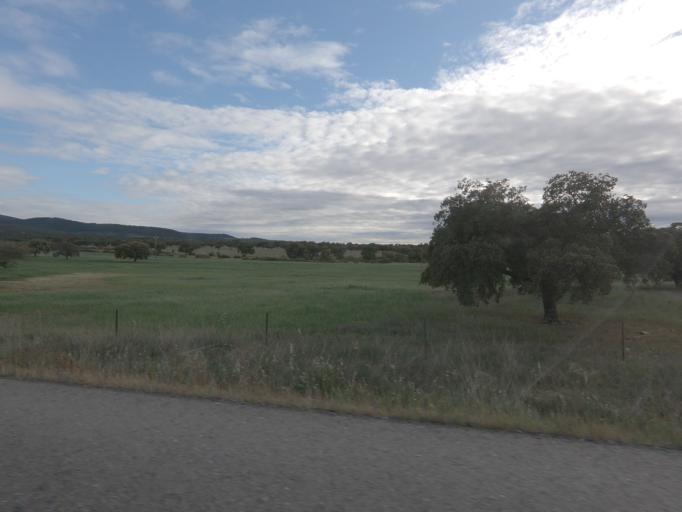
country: ES
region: Extremadura
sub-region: Provincia de Caceres
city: Pedroso de Acim
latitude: 39.8620
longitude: -6.4305
